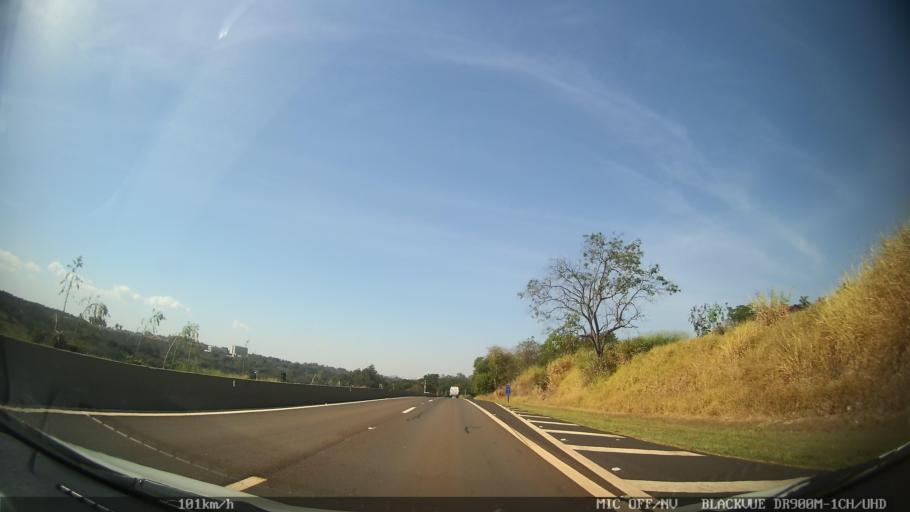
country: BR
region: Sao Paulo
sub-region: Ribeirao Preto
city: Ribeirao Preto
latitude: -21.1672
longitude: -47.8718
